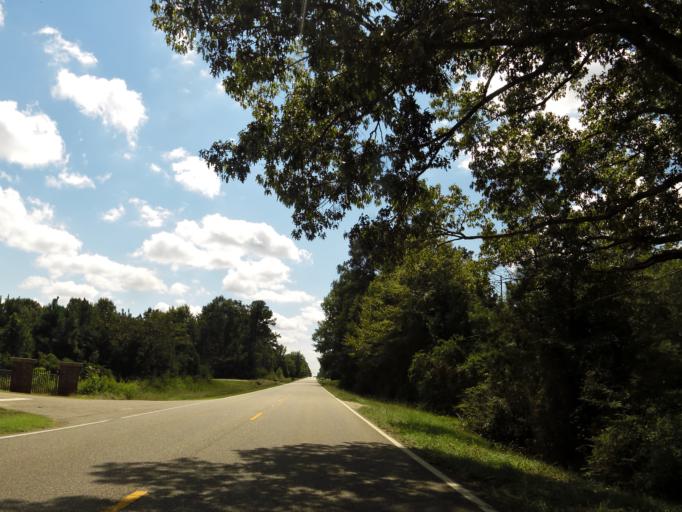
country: US
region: Alabama
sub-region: Dallas County
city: Selma
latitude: 32.4414
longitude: -87.0836
